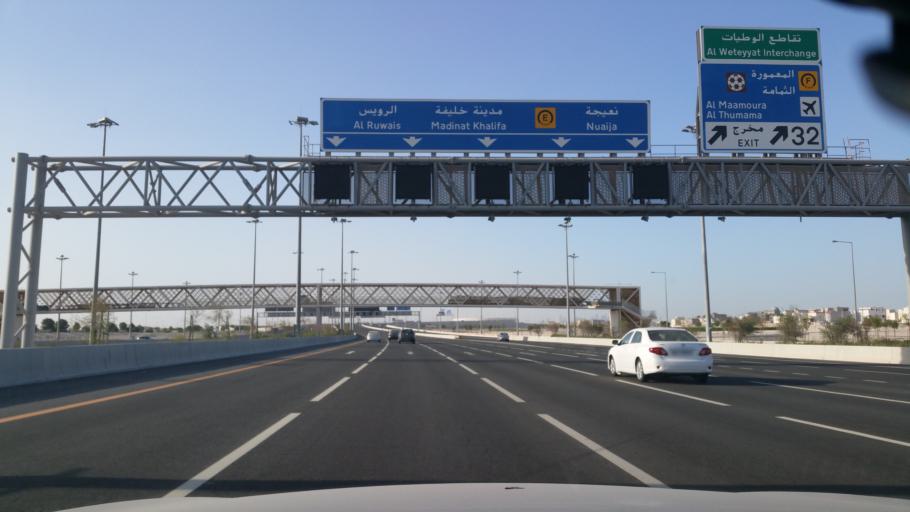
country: QA
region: Al Wakrah
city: Al Wukayr
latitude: 25.2115
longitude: 51.5390
